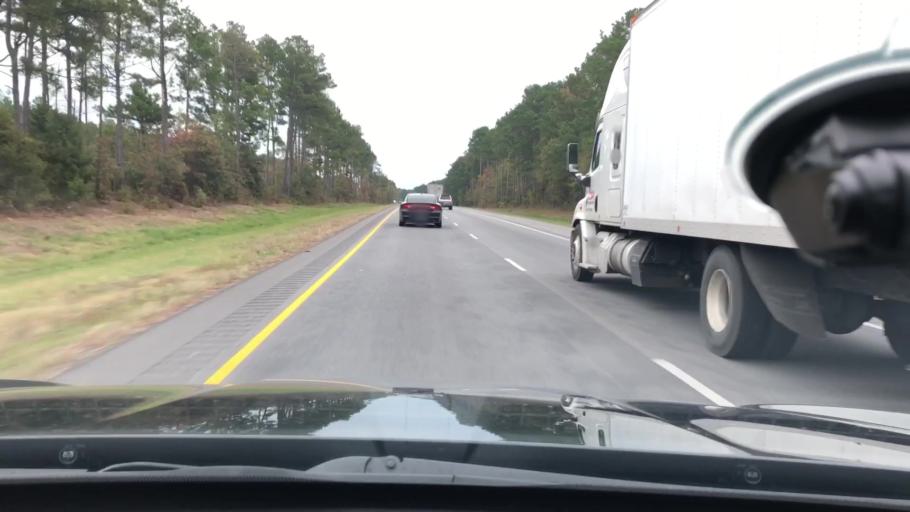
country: US
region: Arkansas
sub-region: Hempstead County
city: Hope
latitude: 33.6273
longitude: -93.7425
